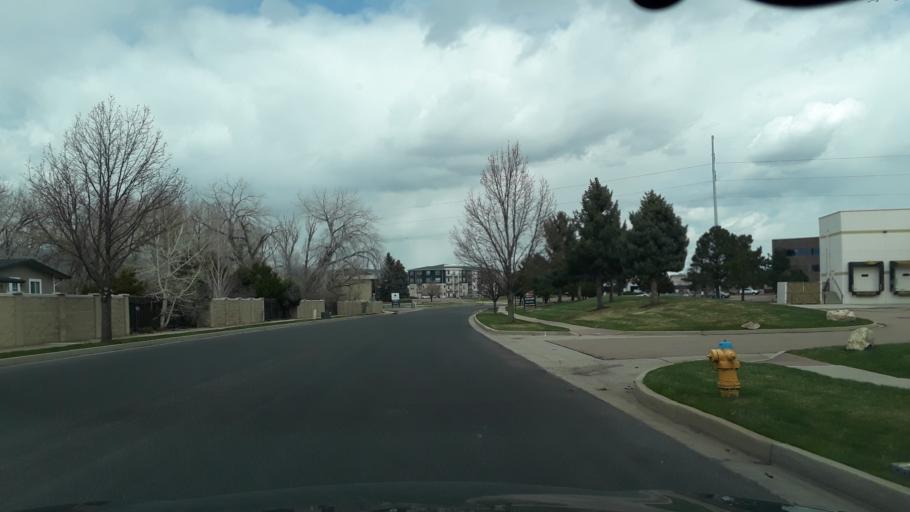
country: US
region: Colorado
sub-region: El Paso County
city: Air Force Academy
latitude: 38.9430
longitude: -104.8035
